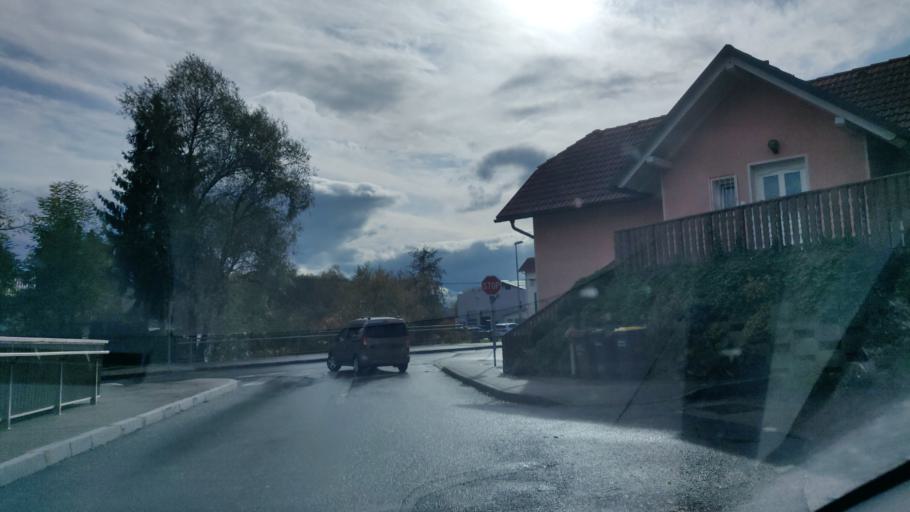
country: SI
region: Trzin
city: Trzin
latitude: 46.1319
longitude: 14.5611
